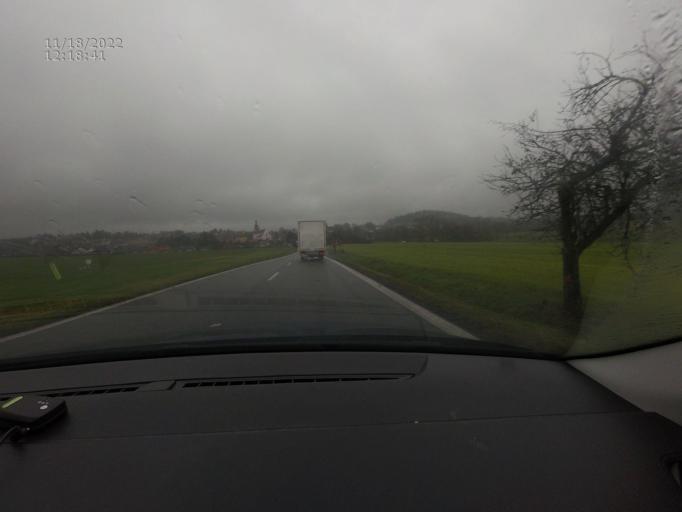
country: CZ
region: Plzensky
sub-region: Okres Plzen-Jih
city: Nepomuk
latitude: 49.4849
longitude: 13.5687
